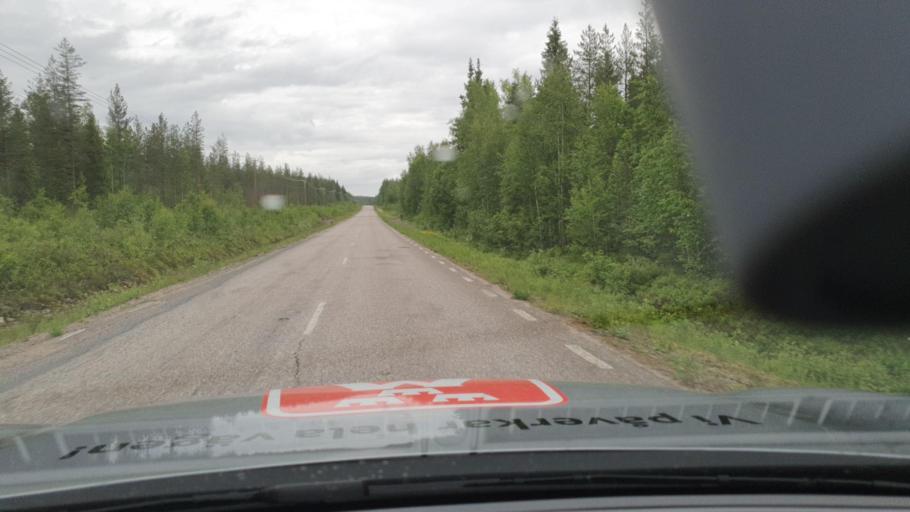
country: SE
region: Norrbotten
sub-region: Overkalix Kommun
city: OEverkalix
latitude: 66.3915
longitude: 22.7912
